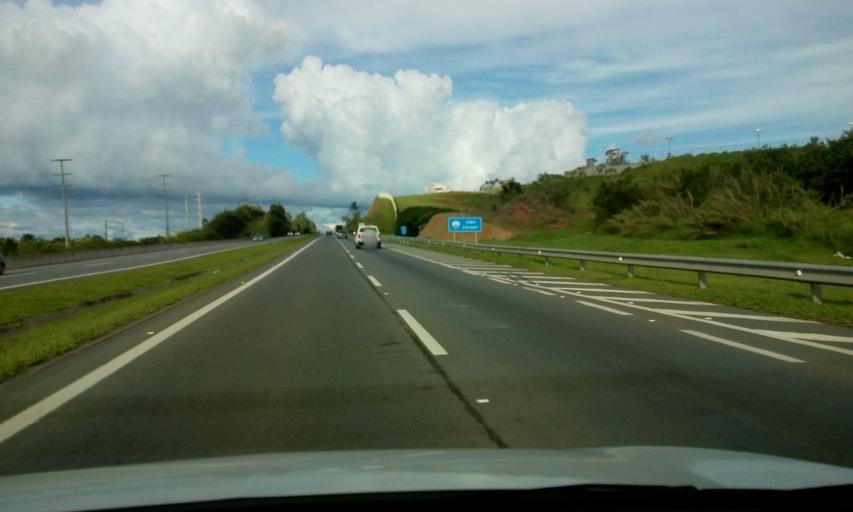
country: BR
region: Sao Paulo
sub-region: Jundiai
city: Jundiai
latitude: -23.1594
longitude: -46.8985
